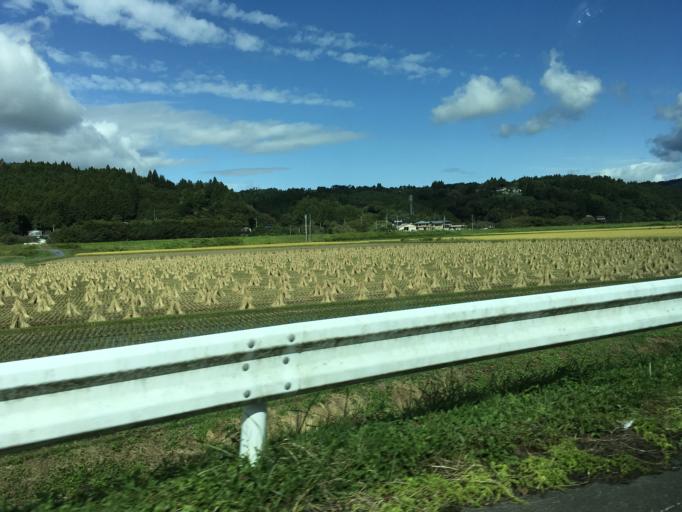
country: JP
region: Iwate
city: Ichinoseki
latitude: 38.8469
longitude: 141.2776
